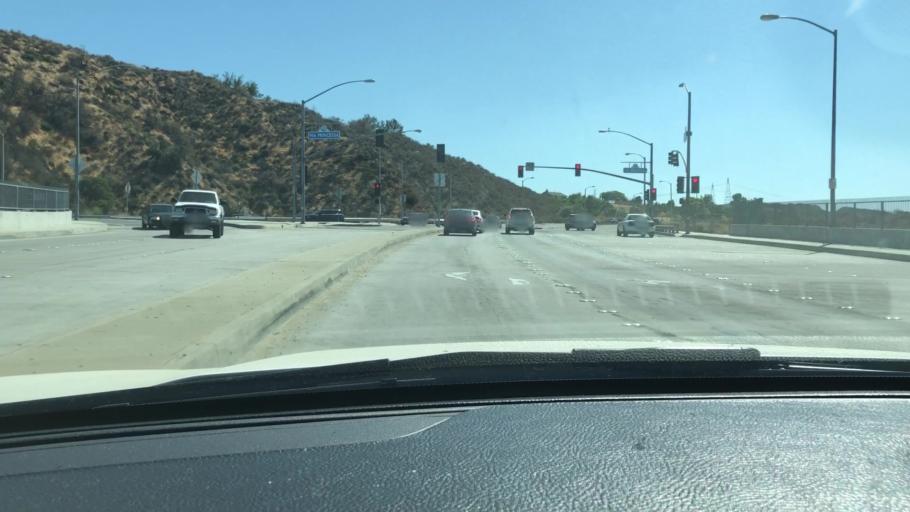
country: US
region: California
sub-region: Los Angeles County
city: Santa Clarita
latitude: 34.4106
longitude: -118.4745
